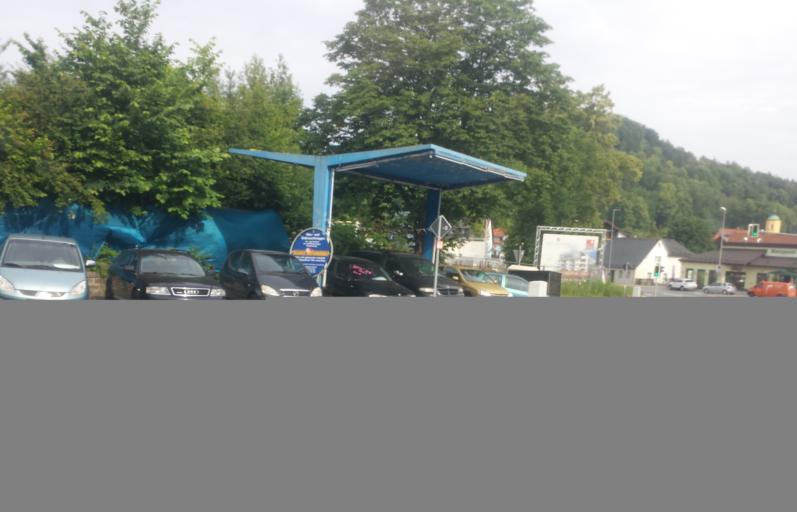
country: DE
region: Bavaria
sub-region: Upper Franconia
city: Pegnitz
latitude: 49.7524
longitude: 11.5386
